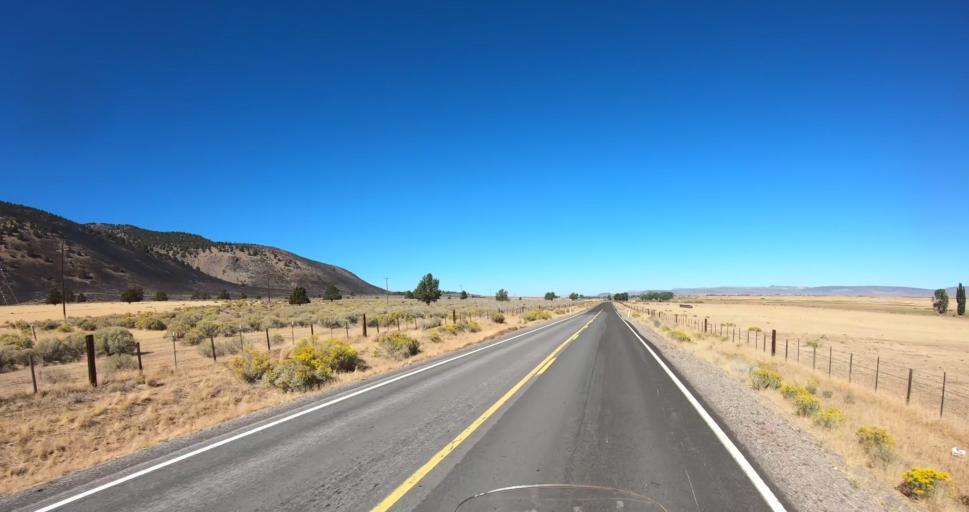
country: US
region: Oregon
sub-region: Lake County
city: Lakeview
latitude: 42.6473
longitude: -120.5212
